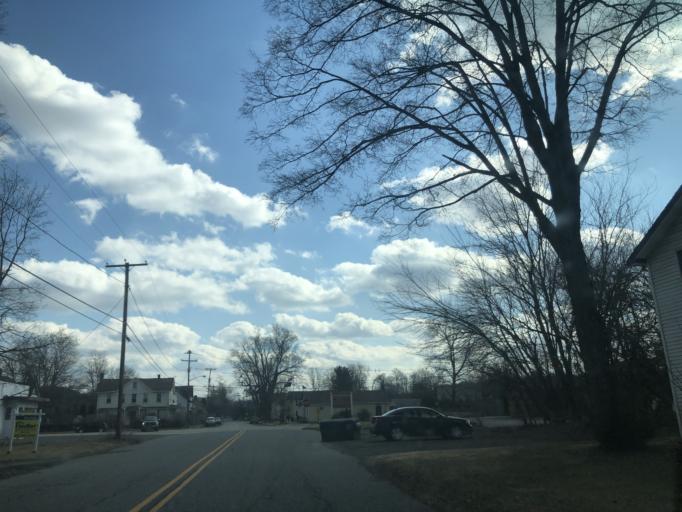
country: US
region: New Jersey
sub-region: Warren County
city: Belvidere
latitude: 40.9273
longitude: -75.0947
